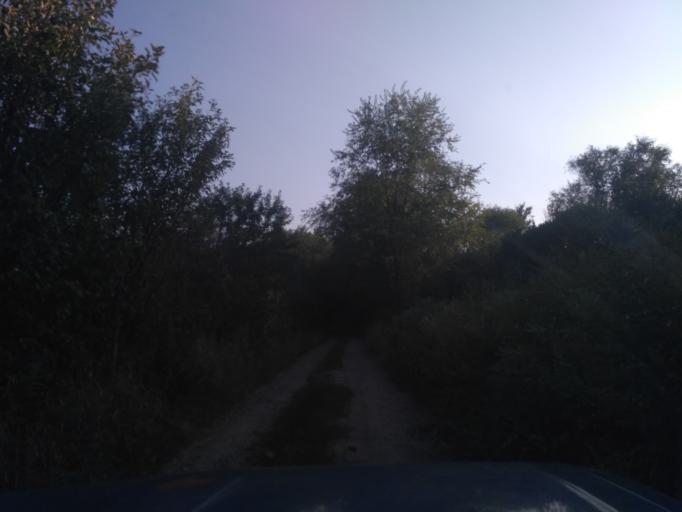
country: KZ
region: Almaty Oblysy
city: Burunday
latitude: 43.1544
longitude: 76.3714
